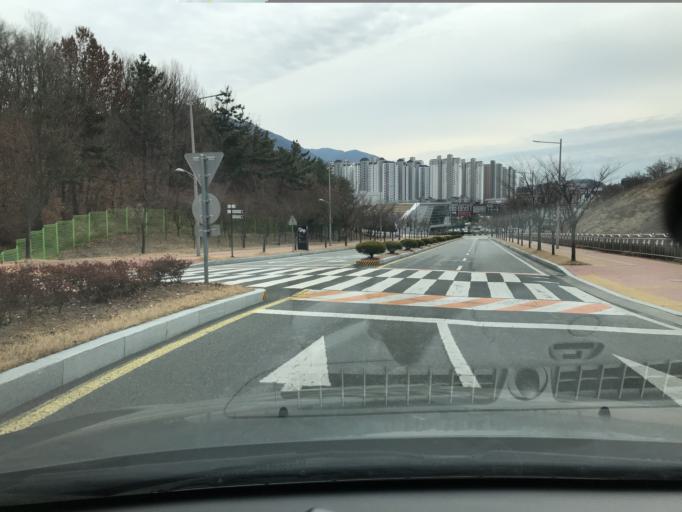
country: KR
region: Daegu
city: Hwawon
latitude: 35.7032
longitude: 128.4578
